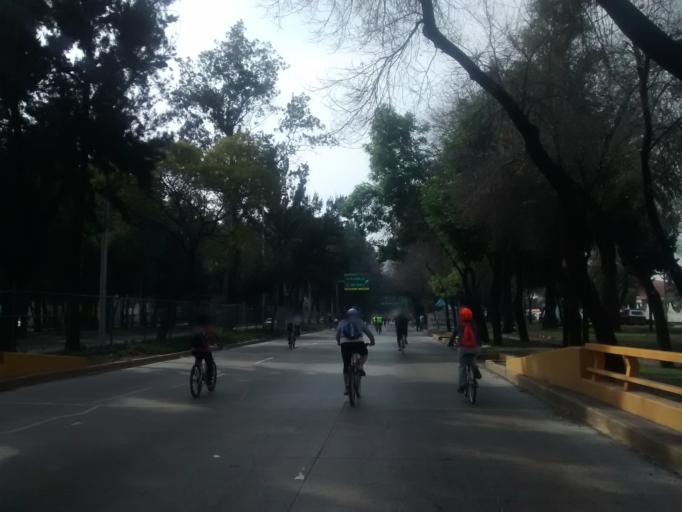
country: MX
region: Mexico City
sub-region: Iztacalco
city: Iztacalco
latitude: 19.3766
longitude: -99.1018
